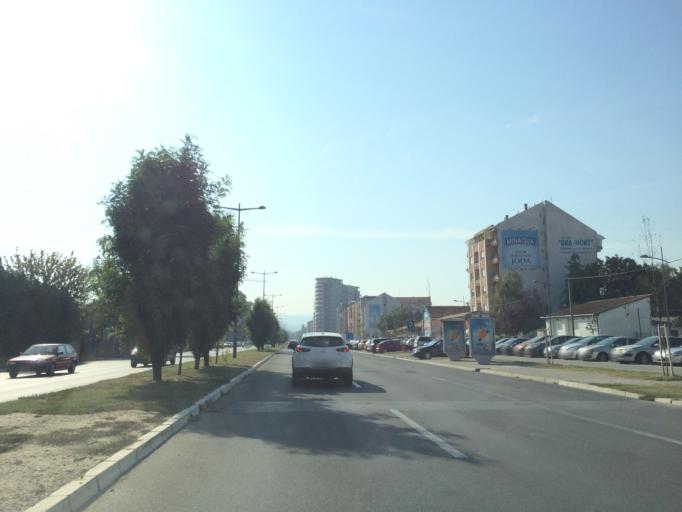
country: RS
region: Autonomna Pokrajina Vojvodina
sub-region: Juznobacki Okrug
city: Novi Sad
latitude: 45.2473
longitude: 19.8174
